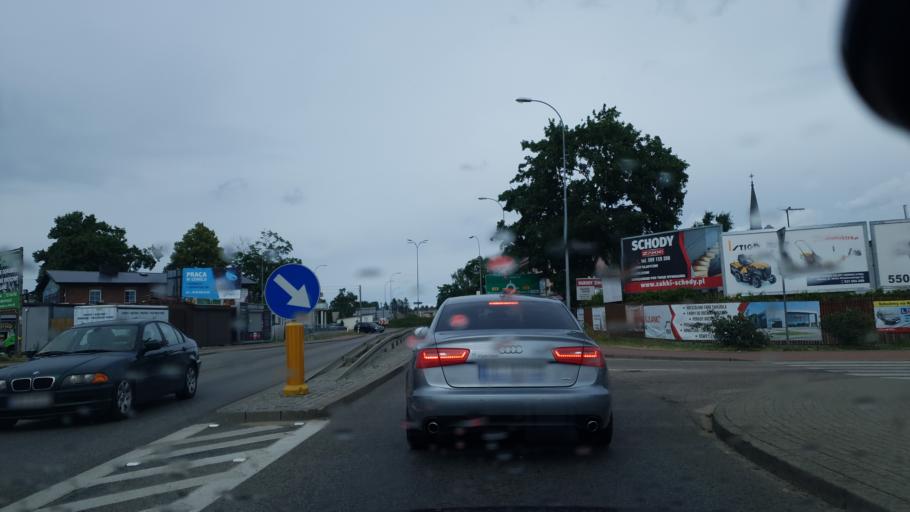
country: PL
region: Pomeranian Voivodeship
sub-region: Powiat kartuski
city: Chwaszczyno
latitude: 54.4428
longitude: 18.4179
